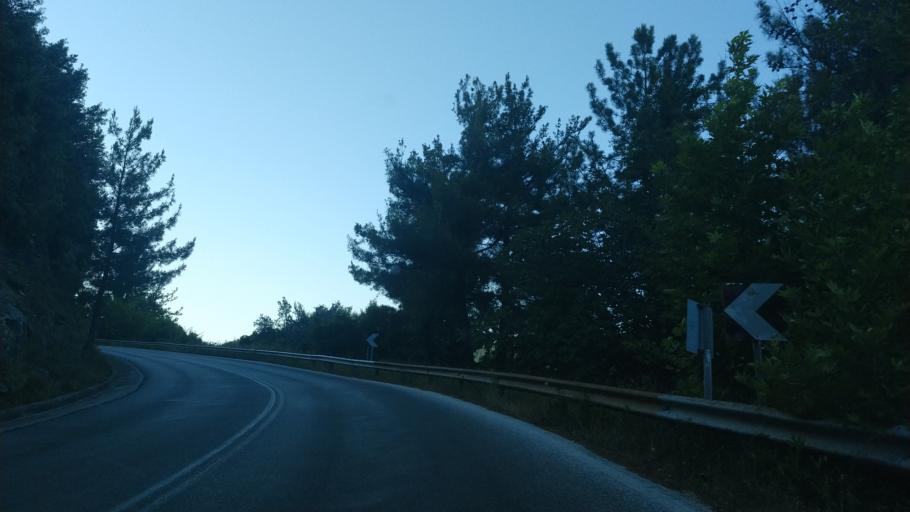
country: GR
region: East Macedonia and Thrace
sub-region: Nomos Kavalas
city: Potamia
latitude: 40.7267
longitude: 24.7335
